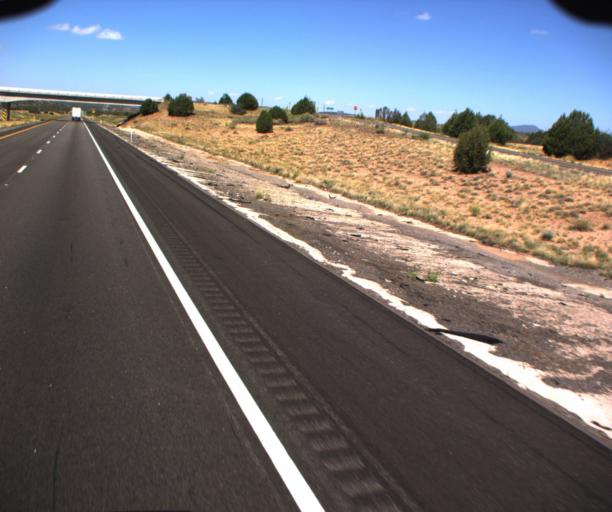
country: US
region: Arizona
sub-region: Mohave County
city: Peach Springs
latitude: 35.1910
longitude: -113.3633
